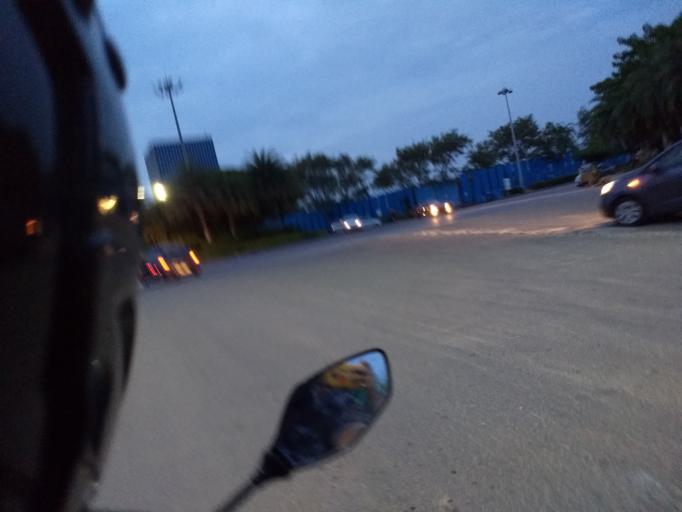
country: IN
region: Telangana
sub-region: Rangareddi
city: Kukatpalli
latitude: 17.4087
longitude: 78.3728
